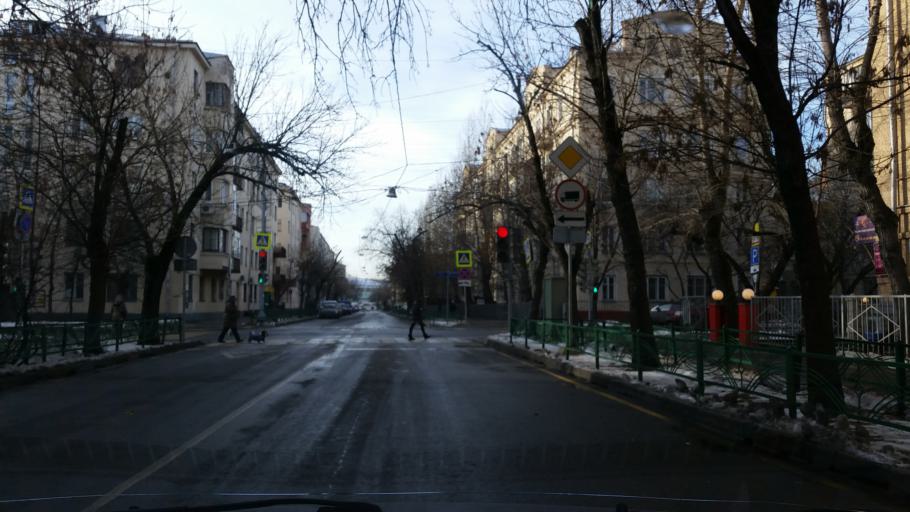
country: RU
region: Moscow
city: Luzhniki
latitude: 55.7244
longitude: 37.5697
